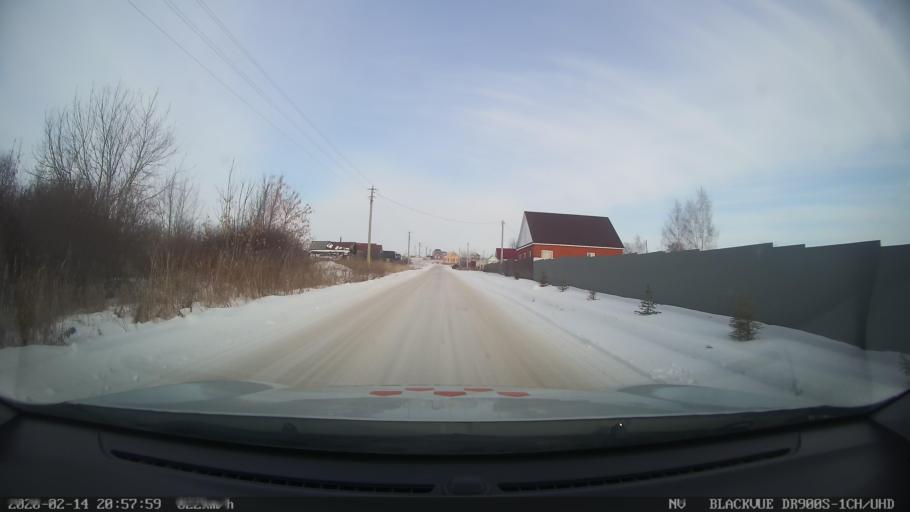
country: RU
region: Tatarstan
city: Kuybyshevskiy Zaton
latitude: 55.1769
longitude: 49.2475
